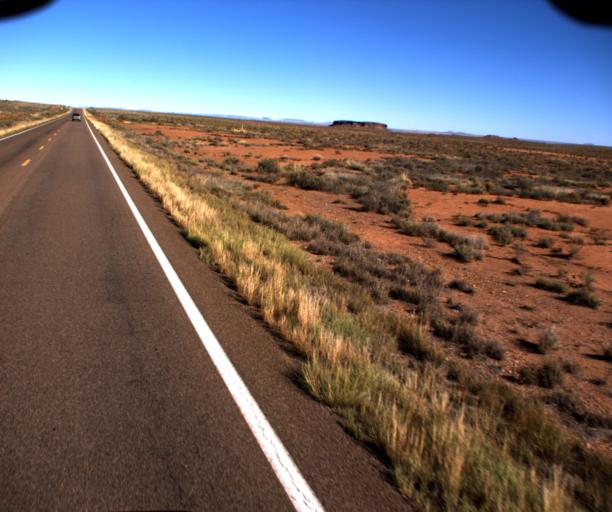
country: US
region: Arizona
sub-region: Navajo County
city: Holbrook
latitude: 34.8204
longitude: -110.1407
